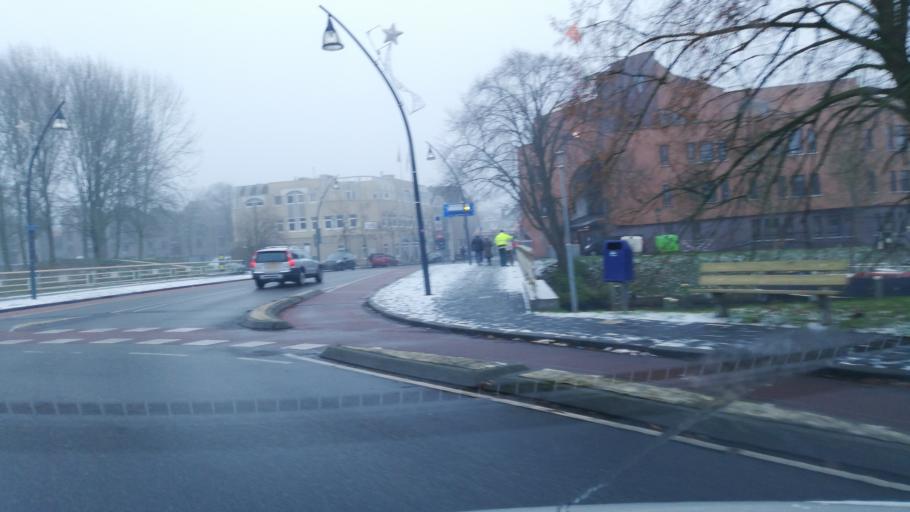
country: NL
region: Overijssel
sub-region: Gemeente Zwolle
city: Zwolle
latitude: 52.5162
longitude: 6.0932
